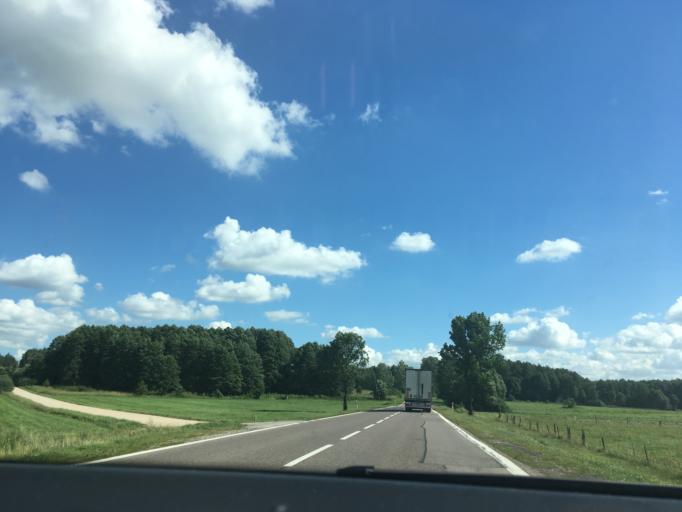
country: PL
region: Podlasie
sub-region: Powiat sokolski
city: Suchowola
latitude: 53.6258
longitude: 23.1225
